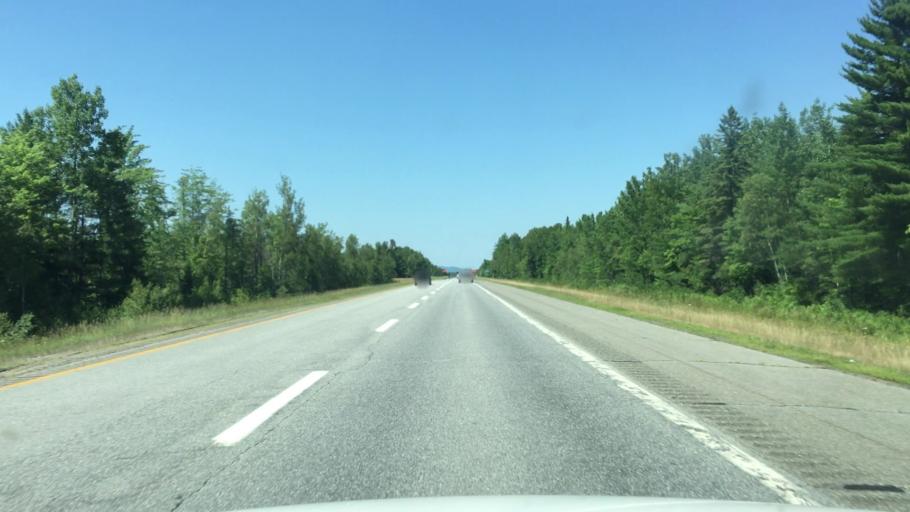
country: US
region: Maine
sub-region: Penobscot County
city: Howland
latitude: 45.2242
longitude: -68.6752
